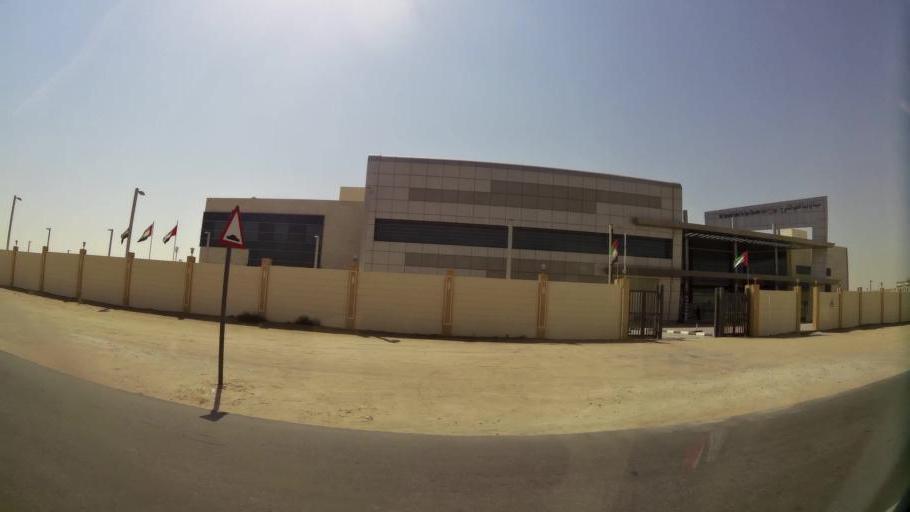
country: AE
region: Ajman
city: Ajman
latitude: 25.4089
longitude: 55.5457
